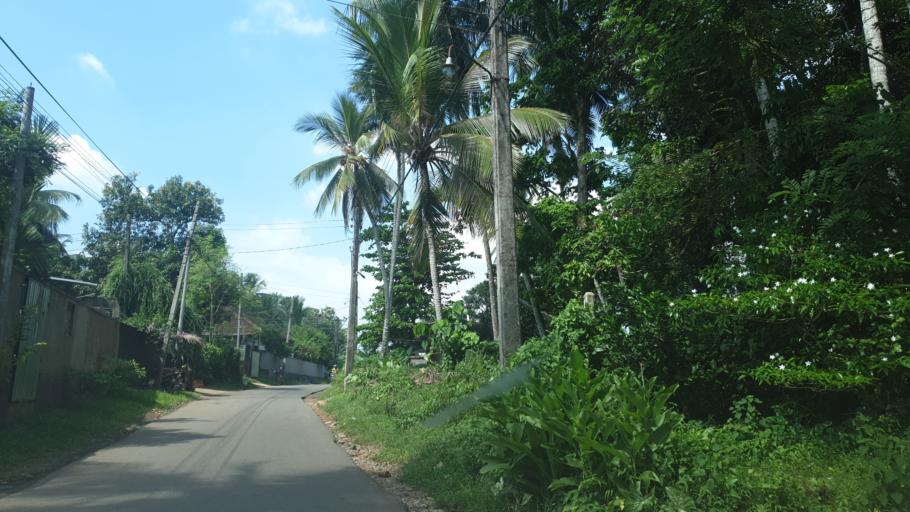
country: LK
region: Western
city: Horana South
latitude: 6.7048
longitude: 79.9850
